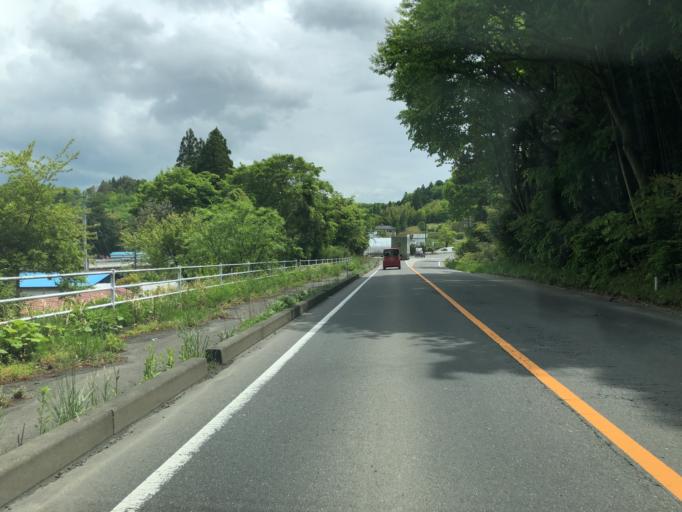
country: JP
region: Fukushima
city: Ishikawa
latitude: 37.0850
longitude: 140.3584
